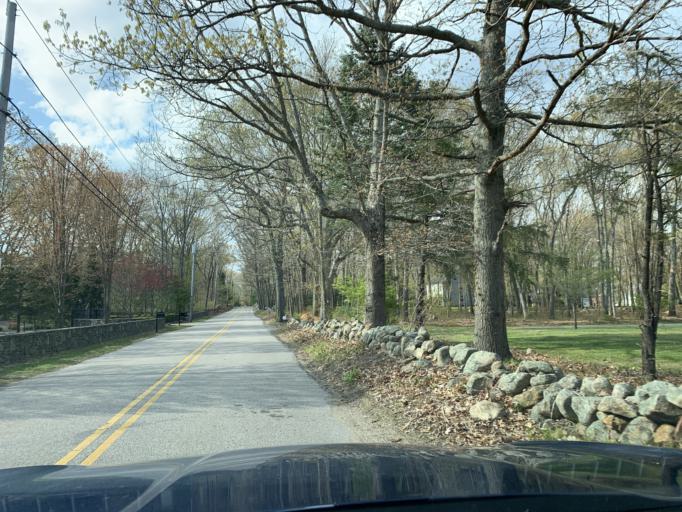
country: US
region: Rhode Island
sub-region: Washington County
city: Exeter
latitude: 41.5948
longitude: -71.5188
